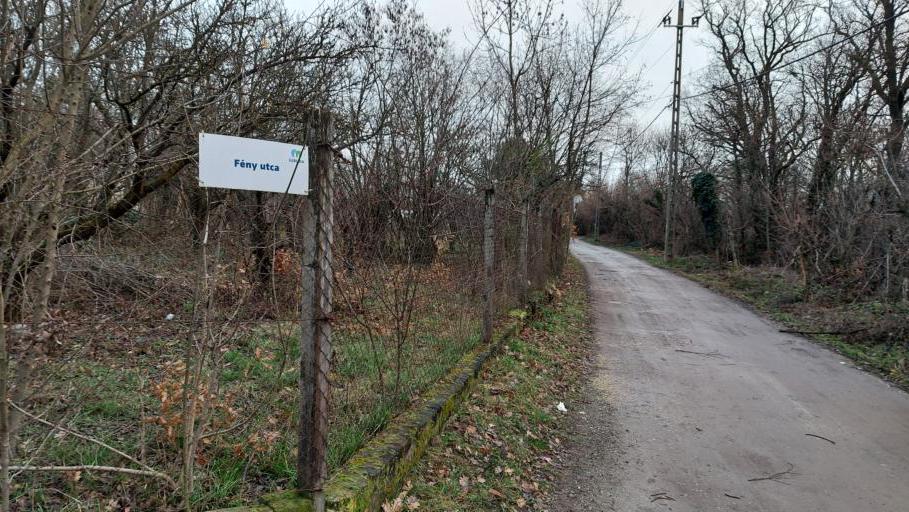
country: HU
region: Pest
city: Budaors
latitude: 47.4342
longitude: 18.9939
